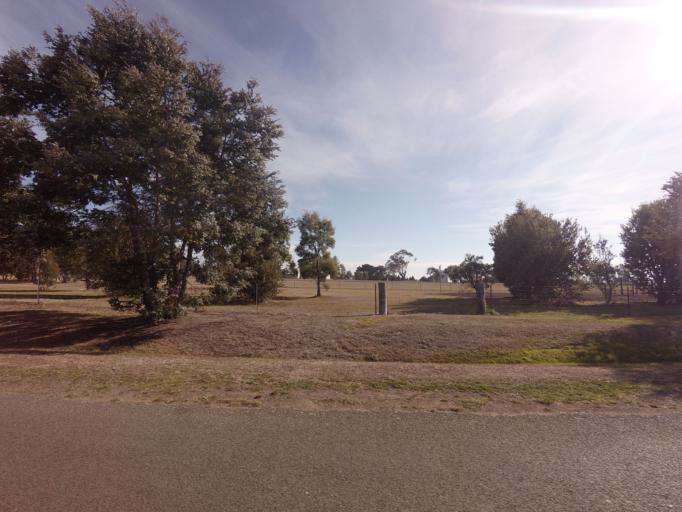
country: AU
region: Tasmania
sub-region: Sorell
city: Sorell
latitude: -42.4552
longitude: 147.4615
